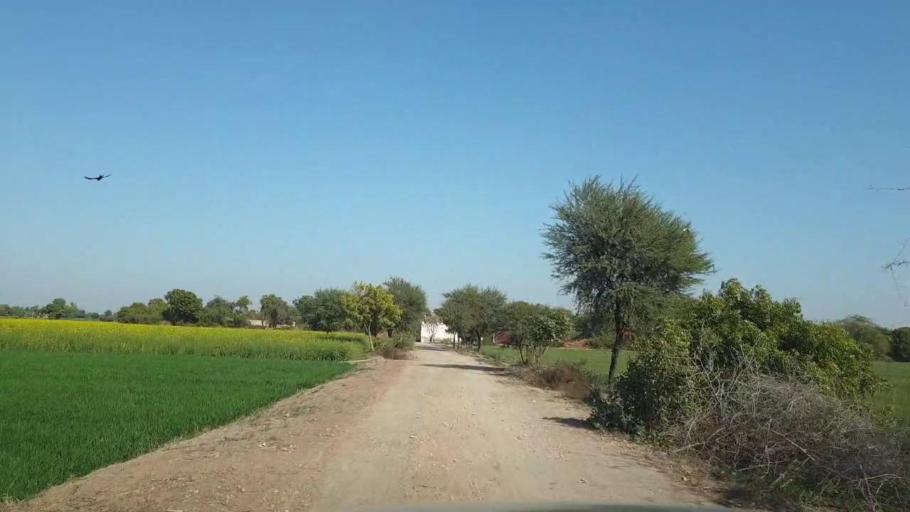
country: PK
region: Sindh
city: Tando Adam
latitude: 25.6711
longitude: 68.6901
